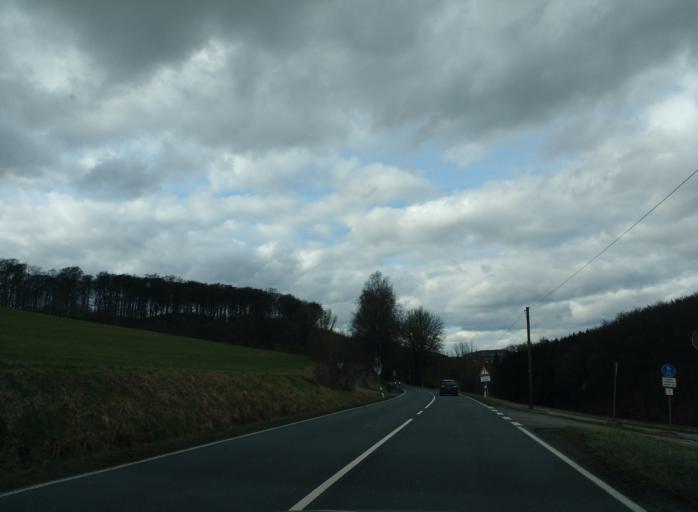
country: DE
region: North Rhine-Westphalia
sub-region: Regierungsbezirk Detmold
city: Lemgo
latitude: 52.0920
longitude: 8.9325
